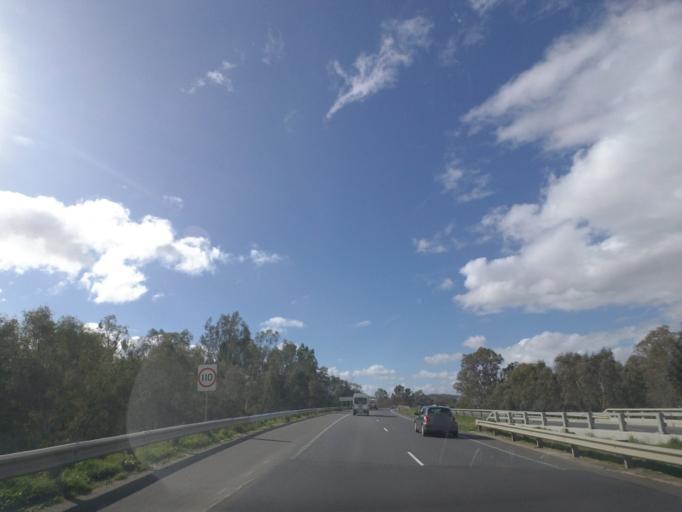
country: AU
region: New South Wales
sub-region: Albury Municipality
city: South Albury
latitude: -36.1019
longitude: 146.9074
